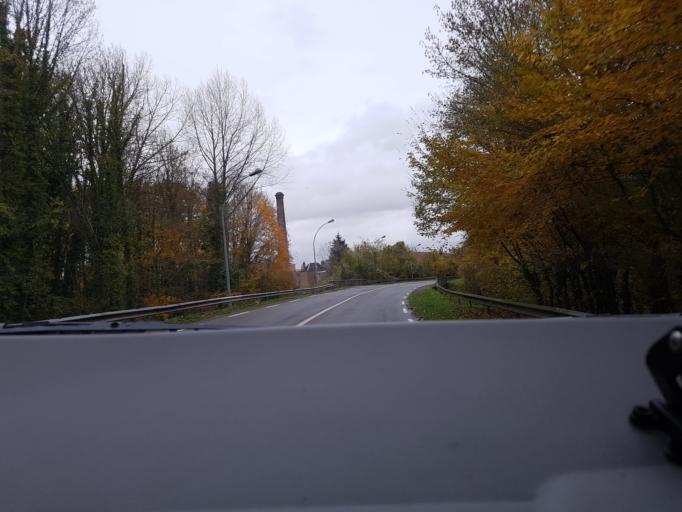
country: FR
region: Picardie
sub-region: Departement de la Somme
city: Abbeville
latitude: 50.1149
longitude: 1.8214
